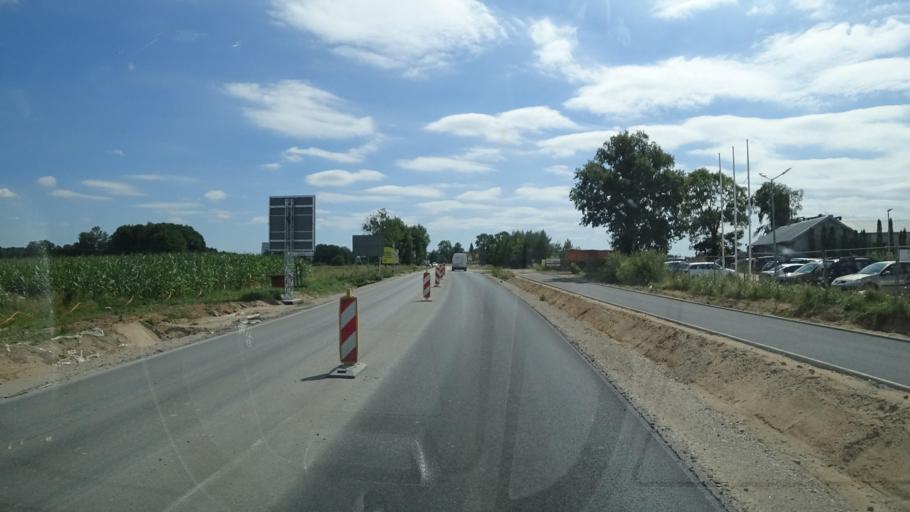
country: PL
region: Warmian-Masurian Voivodeship
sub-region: Powiat elcki
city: Elk
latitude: 53.7503
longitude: 22.3408
